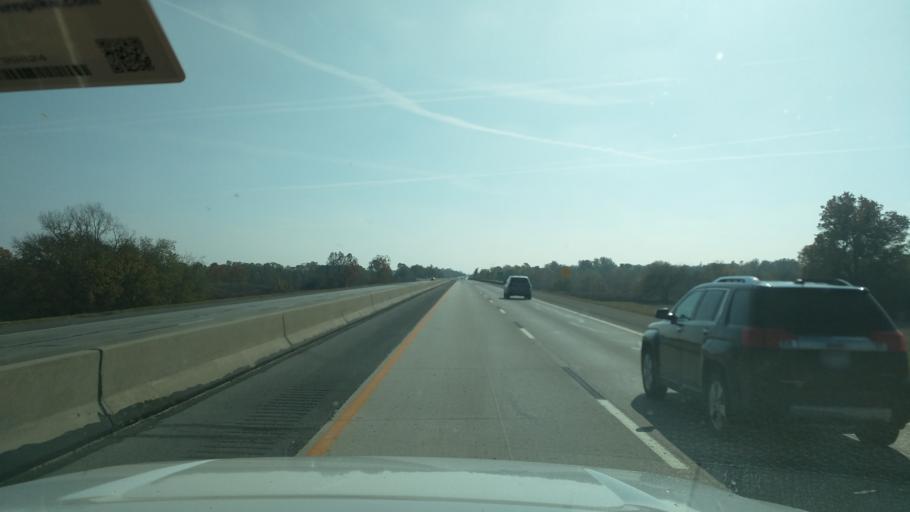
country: US
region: Oklahoma
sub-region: Muskogee County
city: Fort Gibson
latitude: 35.8008
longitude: -95.3184
